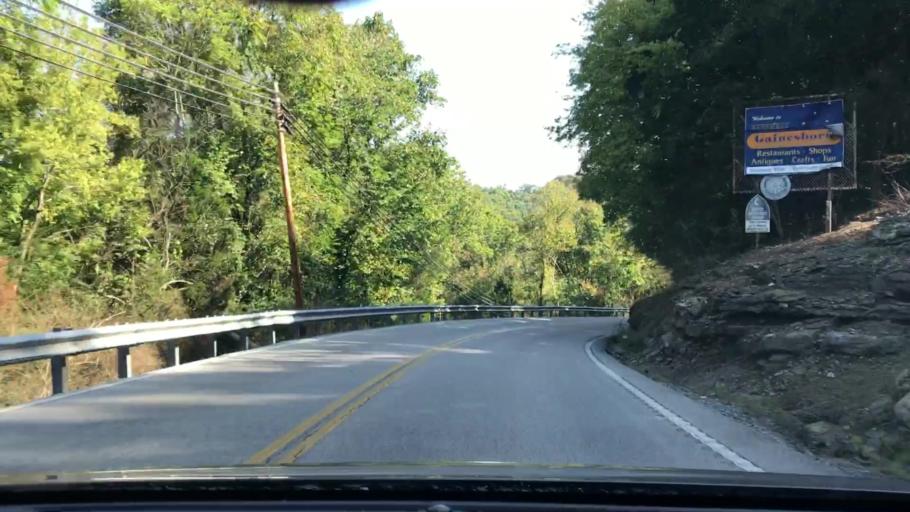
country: US
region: Tennessee
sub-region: Jackson County
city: Gainesboro
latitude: 36.3540
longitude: -85.6666
